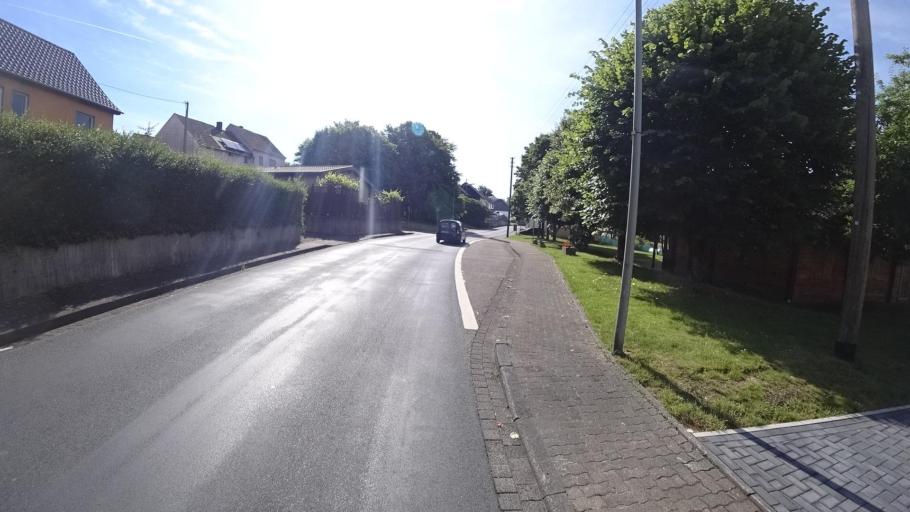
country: DE
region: Rheinland-Pfalz
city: Oberwambach
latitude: 50.6573
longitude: 7.6564
